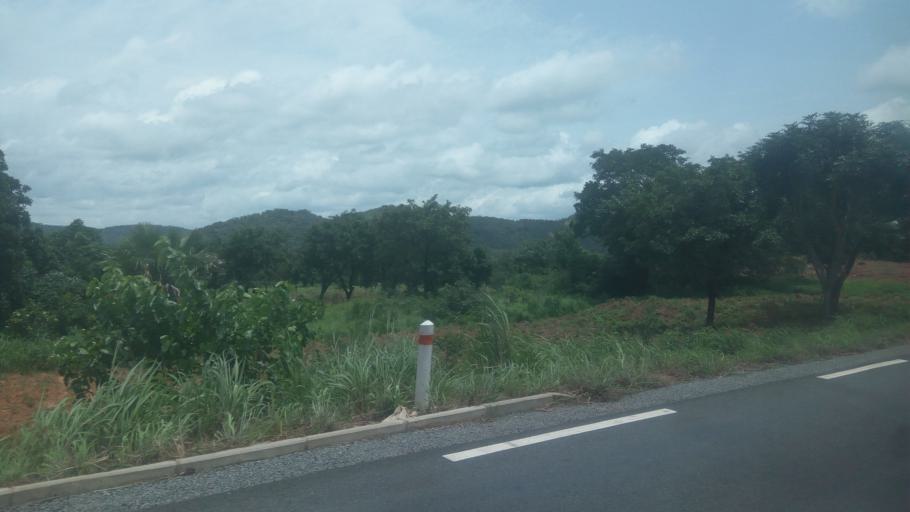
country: TG
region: Kara
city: Bafilo
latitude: 9.2368
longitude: 1.2096
